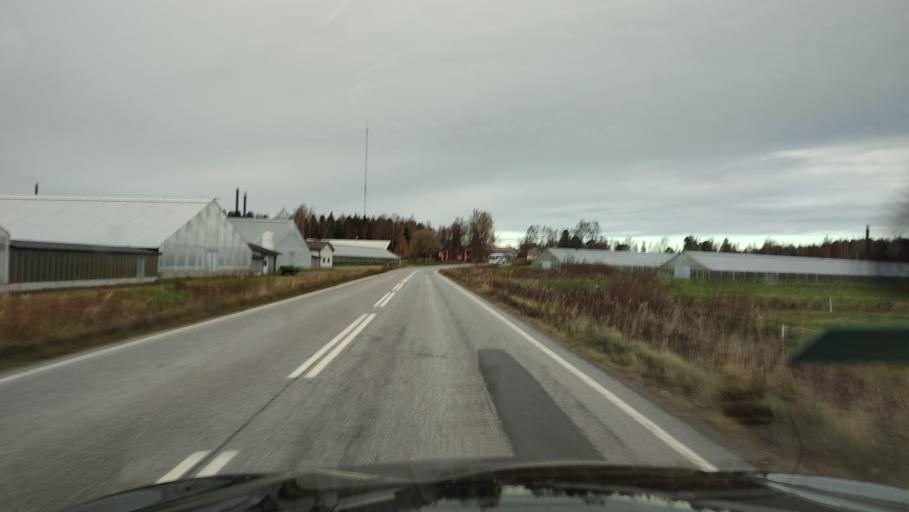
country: FI
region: Ostrobothnia
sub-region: Sydosterbotten
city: Naerpes
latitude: 62.4048
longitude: 21.3524
